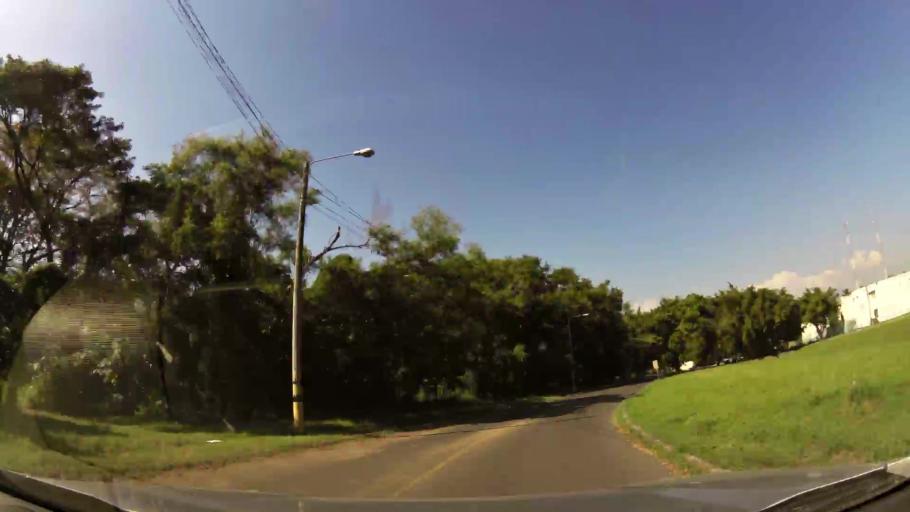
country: GT
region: Escuintla
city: Puerto San Jose
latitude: 13.9347
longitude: -90.7922
